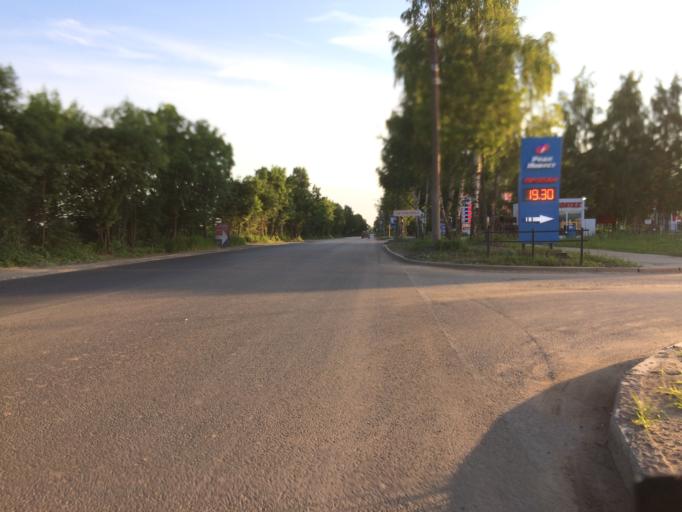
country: RU
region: Mariy-El
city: Medvedevo
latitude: 56.6423
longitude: 47.8316
